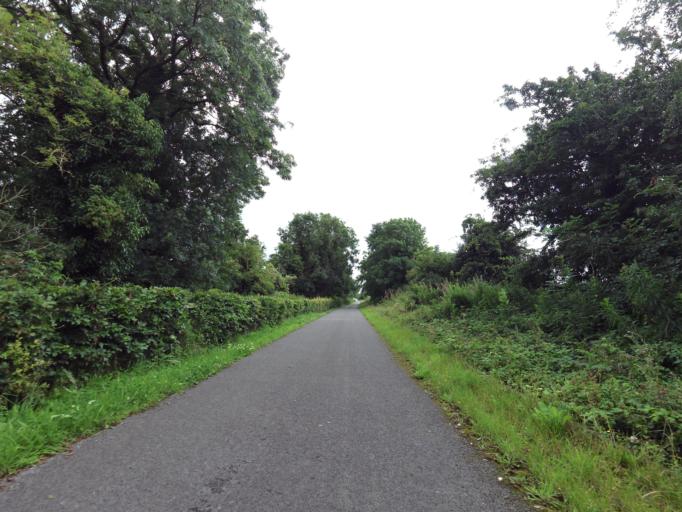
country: IE
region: Leinster
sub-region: An Iarmhi
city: An Muileann gCearr
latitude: 53.5071
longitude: -7.4180
